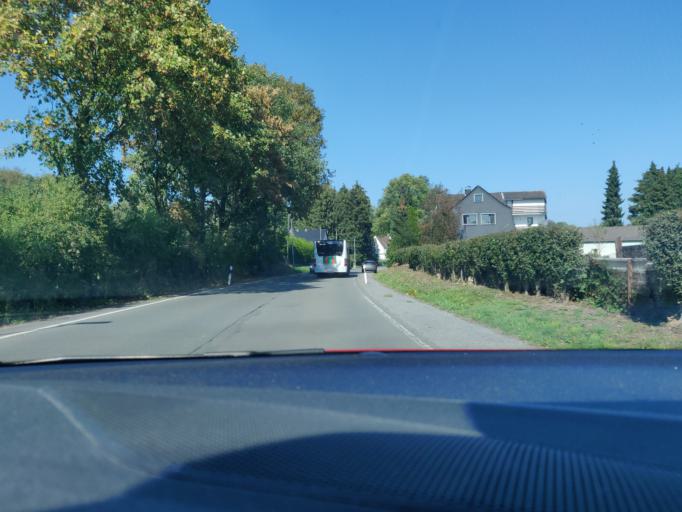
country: DE
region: North Rhine-Westphalia
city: Sprockhovel
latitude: 51.3377
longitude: 7.2408
